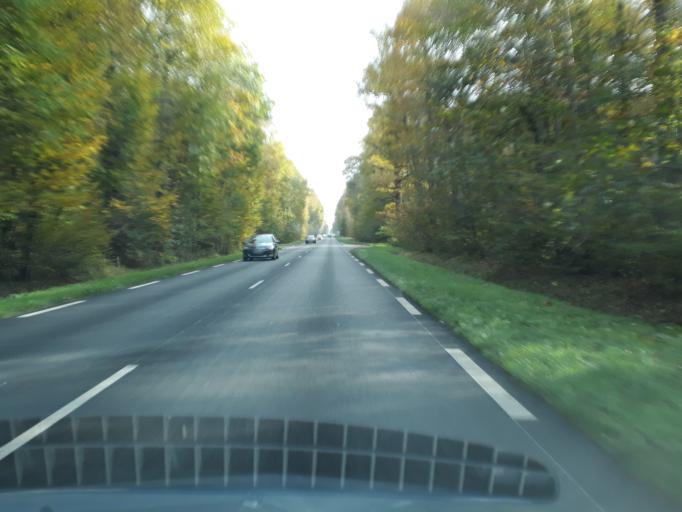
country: FR
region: Ile-de-France
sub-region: Departement de Seine-et-Marne
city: Thomery
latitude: 48.4210
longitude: 2.7822
